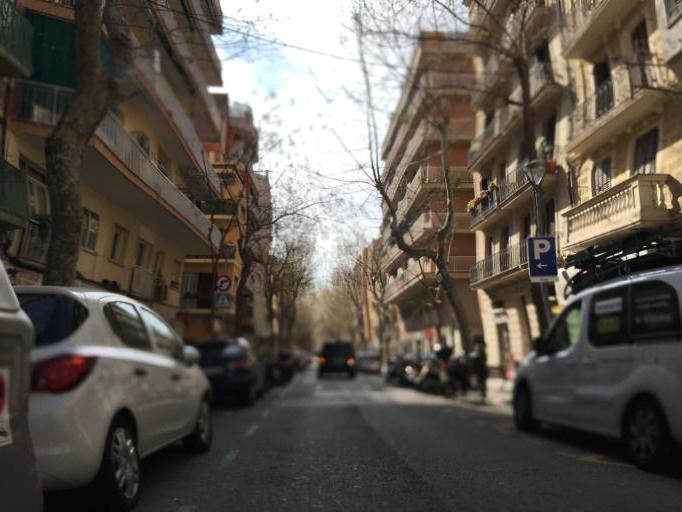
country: ES
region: Catalonia
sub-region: Provincia de Barcelona
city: les Corts
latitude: 41.3812
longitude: 2.1359
